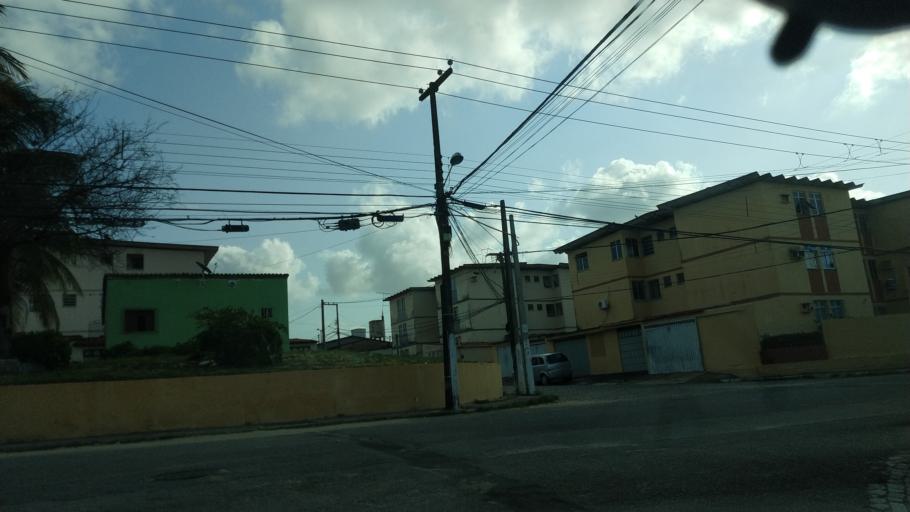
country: BR
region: Rio Grande do Norte
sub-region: Natal
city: Natal
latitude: -5.8628
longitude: -35.2022
